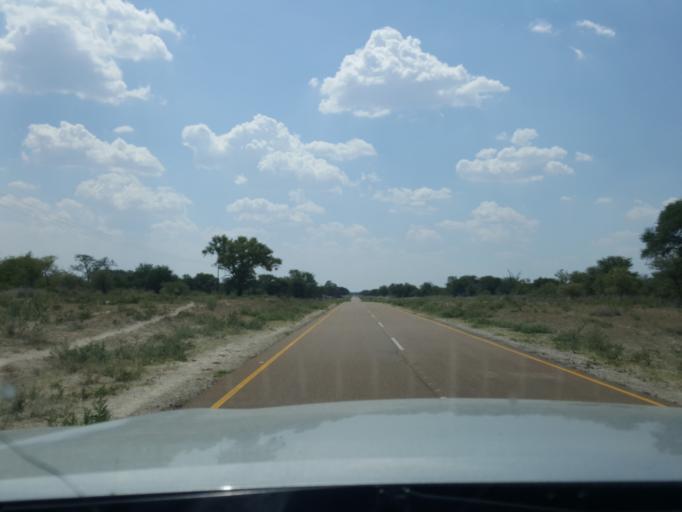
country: BW
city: Nokaneng
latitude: -19.8252
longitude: 22.2243
